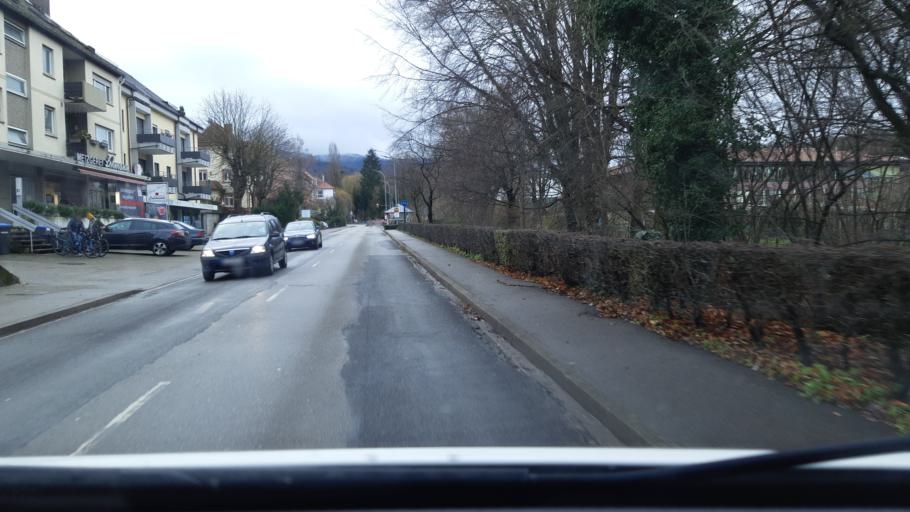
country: DE
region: Baden-Wuerttemberg
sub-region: Freiburg Region
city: Merzhausen
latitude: 47.9682
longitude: 7.8285
